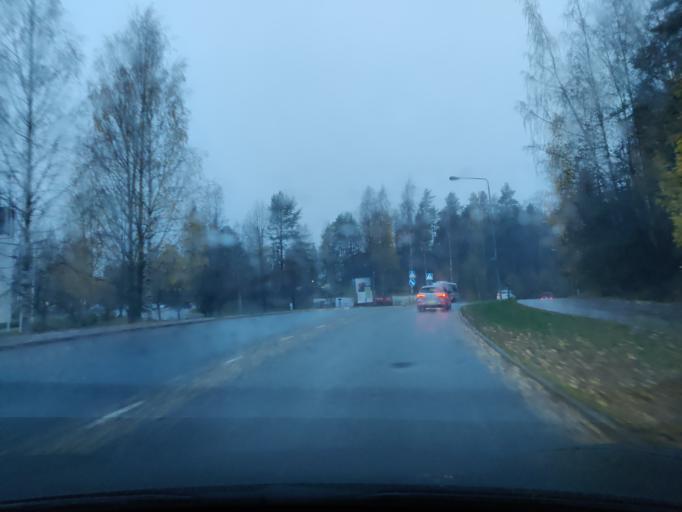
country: FI
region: Northern Savo
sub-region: Kuopio
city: Kuopio
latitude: 62.8479
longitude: 27.6427
